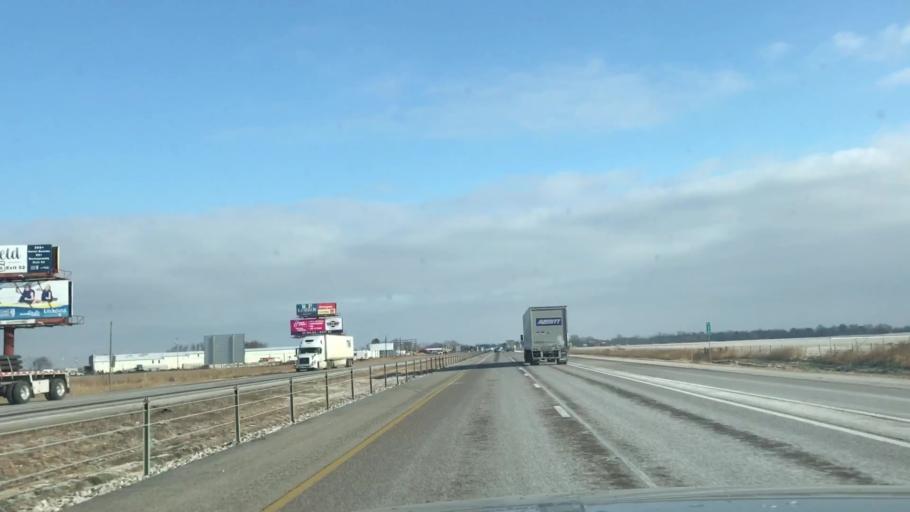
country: US
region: Illinois
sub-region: Madison County
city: Worden
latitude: 38.8921
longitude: -89.8360
